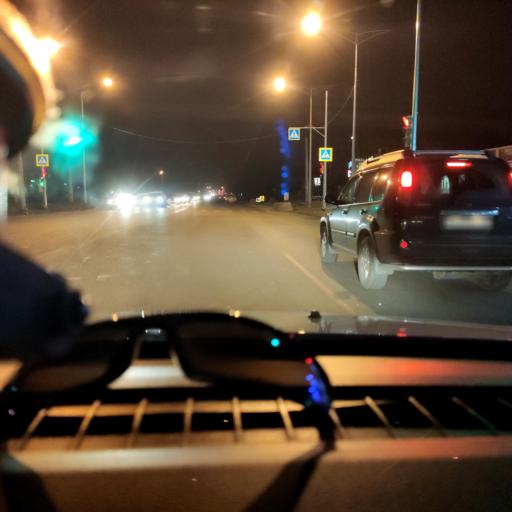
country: RU
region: Samara
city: Samara
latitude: 53.1271
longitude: 50.0902
